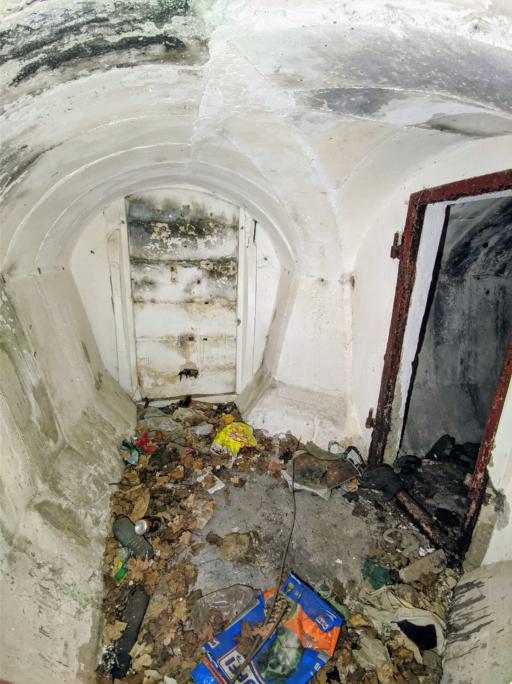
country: PL
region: Lubusz
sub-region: Powiat zaganski
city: Zagan
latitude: 51.6036
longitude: 15.3135
